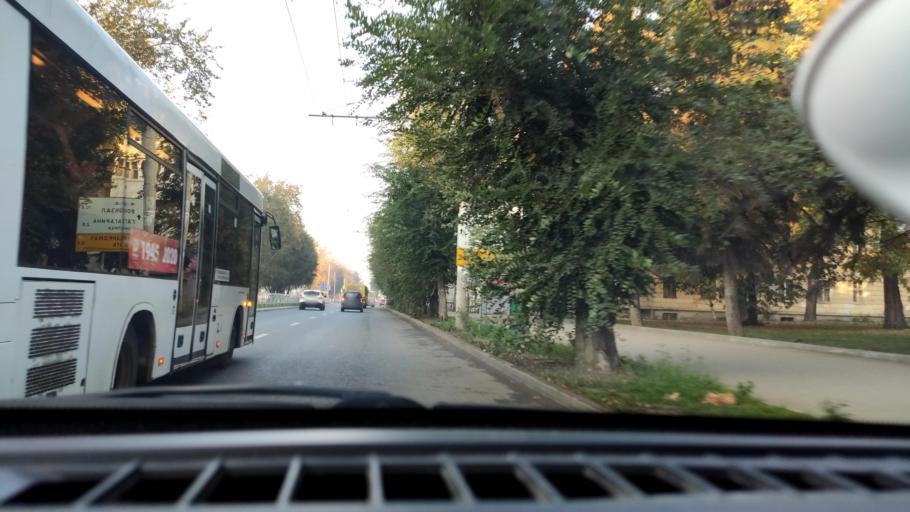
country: RU
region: Samara
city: Samara
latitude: 53.2173
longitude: 50.2580
